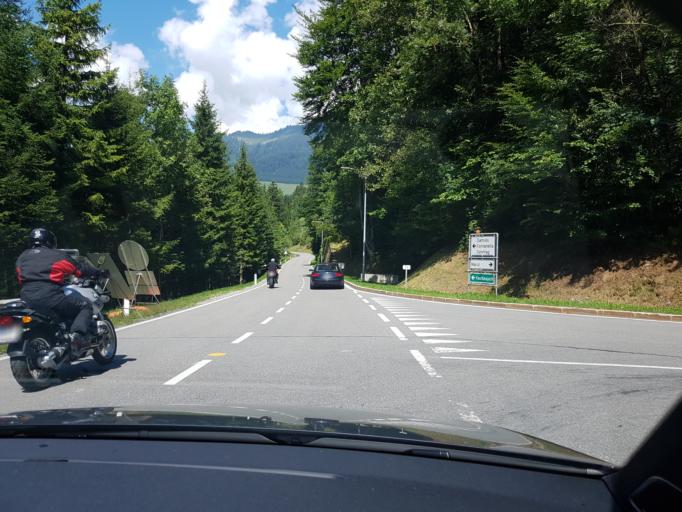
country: AT
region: Vorarlberg
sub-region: Politischer Bezirk Bludenz
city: Raggal
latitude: 47.2083
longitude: 9.8543
